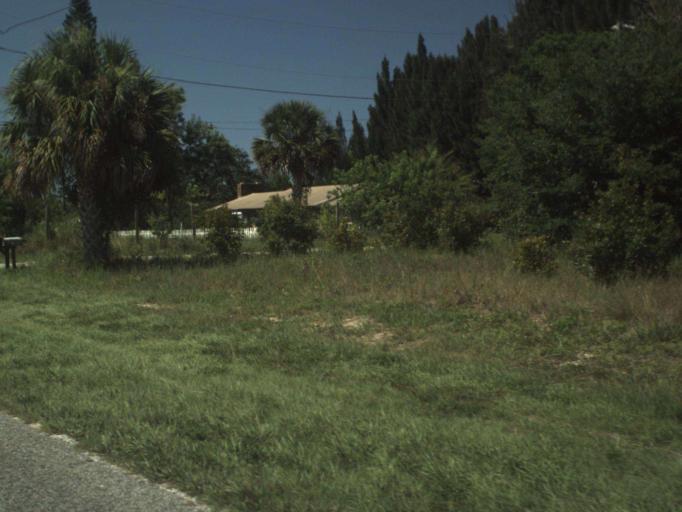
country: US
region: Florida
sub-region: Indian River County
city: Winter Beach
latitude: 27.6993
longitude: -80.4153
